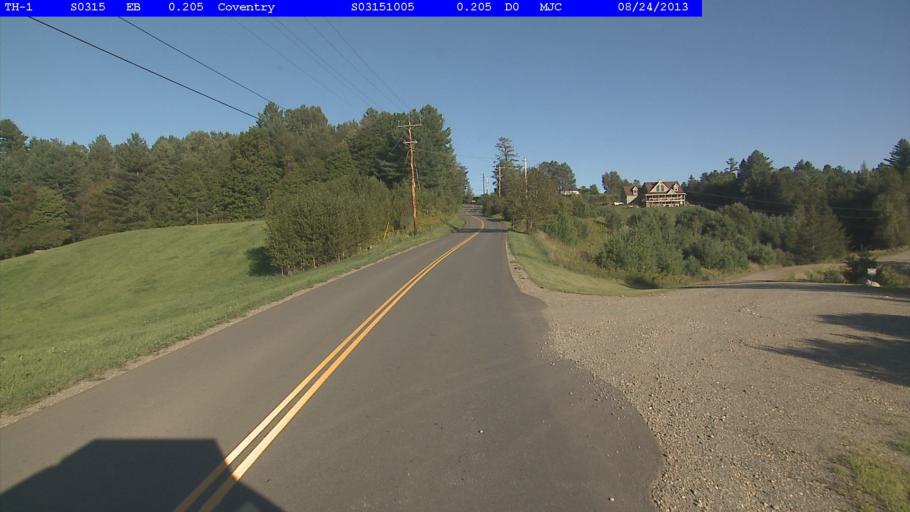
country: US
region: Vermont
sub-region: Orleans County
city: Newport
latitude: 44.8679
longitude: -72.2562
